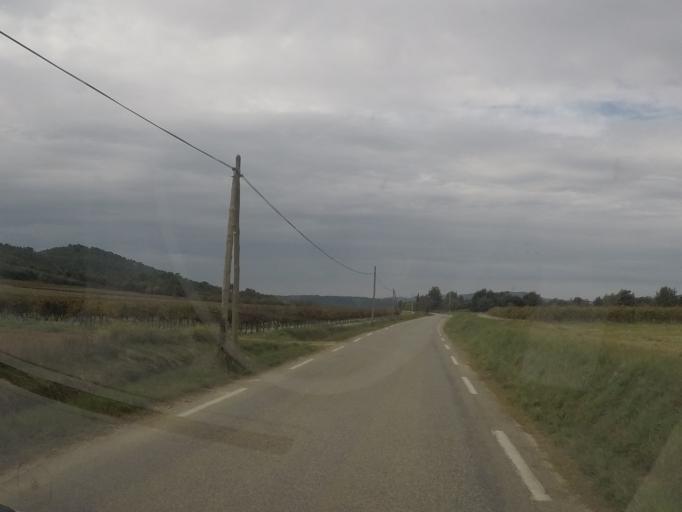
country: FR
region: Provence-Alpes-Cote d'Azur
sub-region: Departement du Vaucluse
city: Villelaure
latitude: 43.7434
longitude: 5.4273
